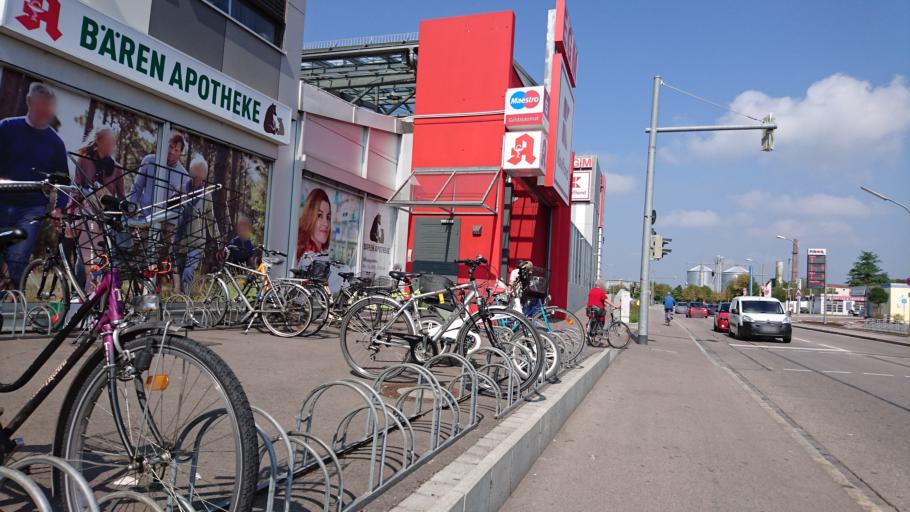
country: DE
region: Bavaria
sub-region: Swabia
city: Augsburg
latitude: 48.3803
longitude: 10.9325
